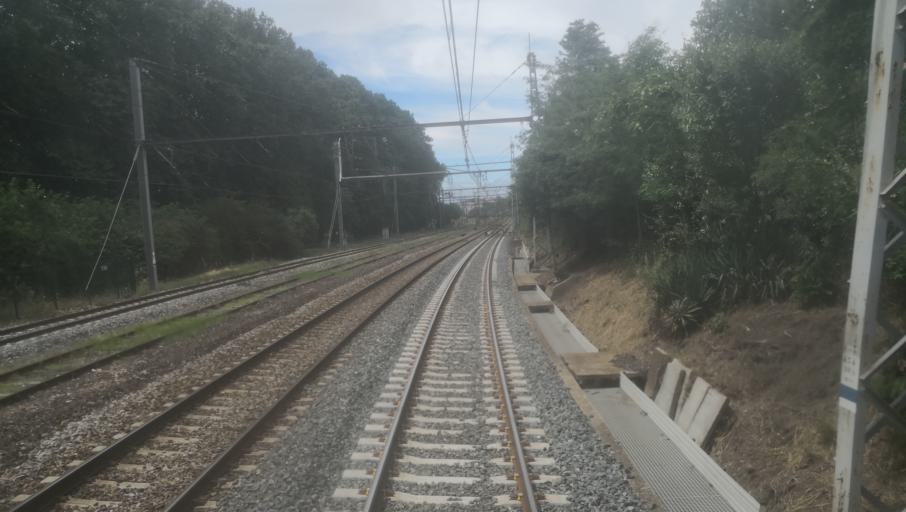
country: FR
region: Languedoc-Roussillon
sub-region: Departement de l'Herault
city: Sauvian
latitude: 43.3256
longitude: 3.2464
